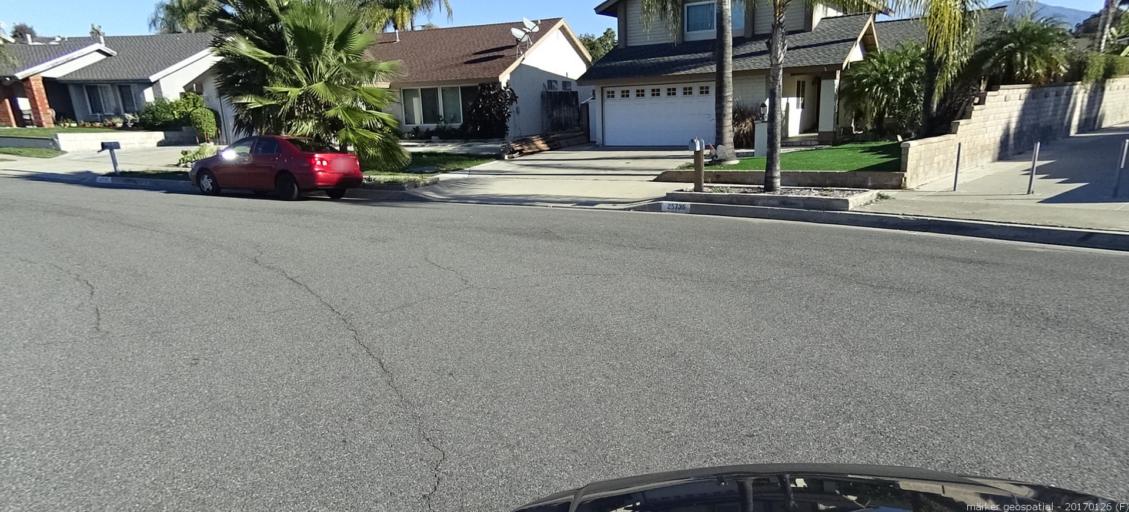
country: US
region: California
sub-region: Orange County
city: Lake Forest
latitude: 33.6331
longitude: -117.6817
